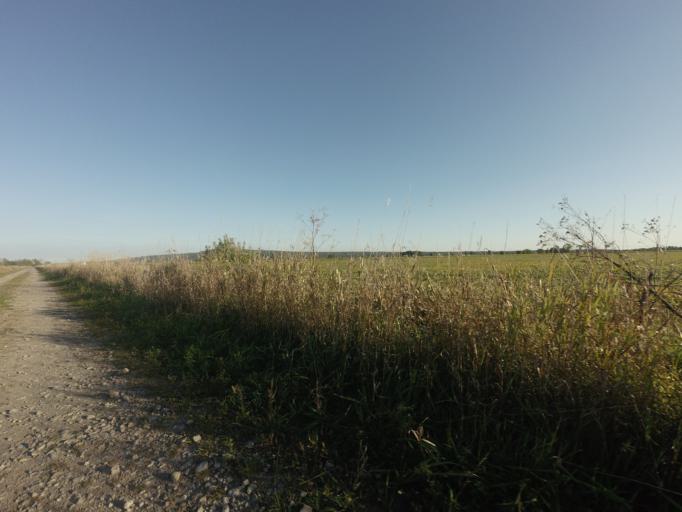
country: CA
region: Quebec
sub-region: Monteregie
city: Rigaud
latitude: 45.4866
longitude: -74.3642
